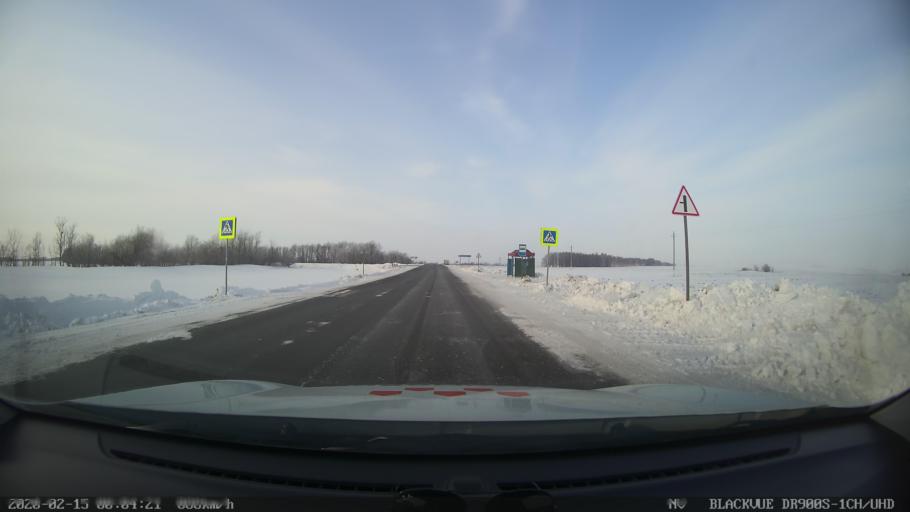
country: RU
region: Tatarstan
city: Kuybyshevskiy Zaton
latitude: 55.3815
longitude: 48.9846
